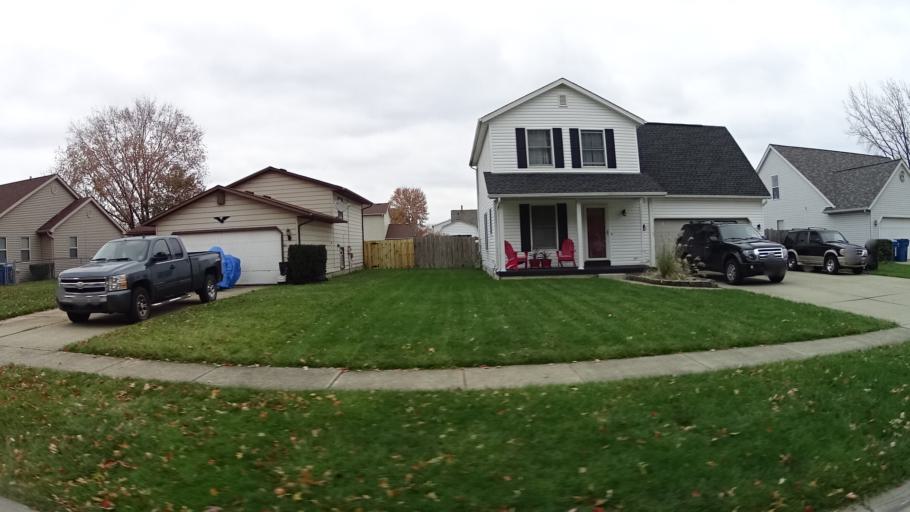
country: US
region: Ohio
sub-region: Lorain County
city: Lorain
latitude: 41.4353
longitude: -82.2128
